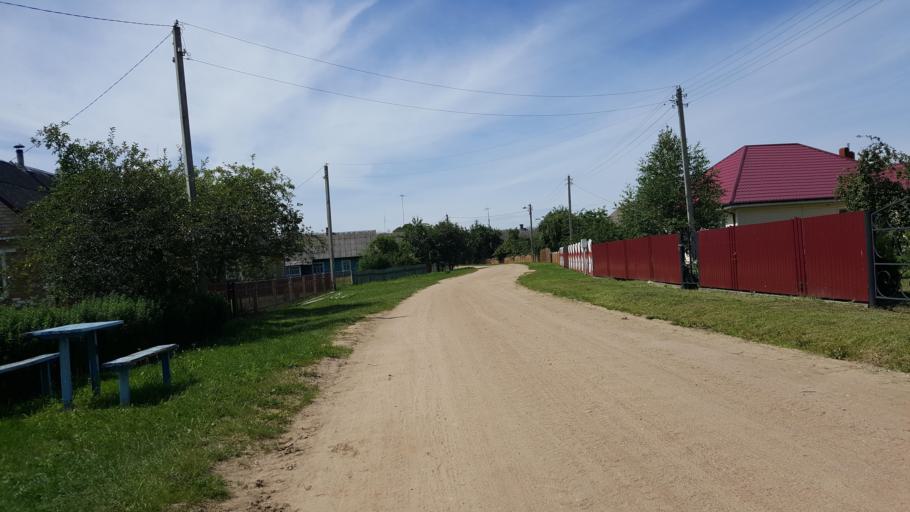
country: BY
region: Brest
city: Pruzhany
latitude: 52.5641
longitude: 24.2196
